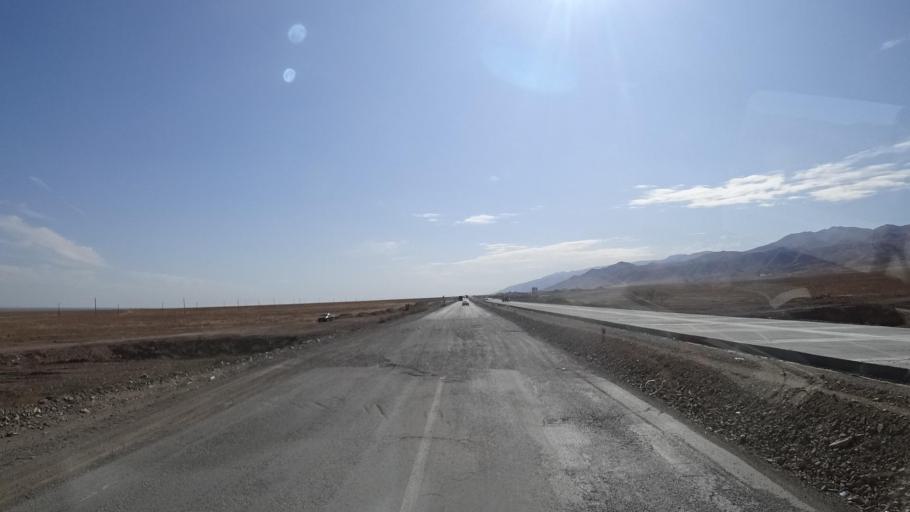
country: KG
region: Chuy
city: Ivanovka
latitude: 43.3970
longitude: 75.1239
